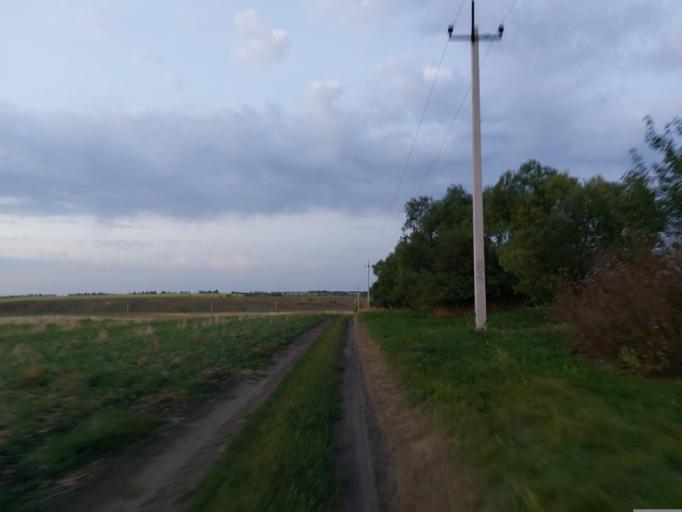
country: RU
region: Lipetsk
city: Dolgorukovo
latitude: 52.3821
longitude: 38.0461
